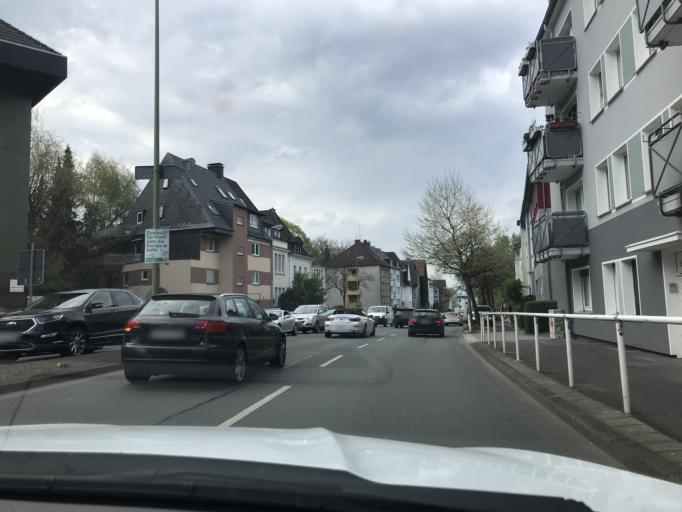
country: DE
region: North Rhine-Westphalia
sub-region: Regierungsbezirk Dusseldorf
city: Essen
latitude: 51.4404
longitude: 7.0221
